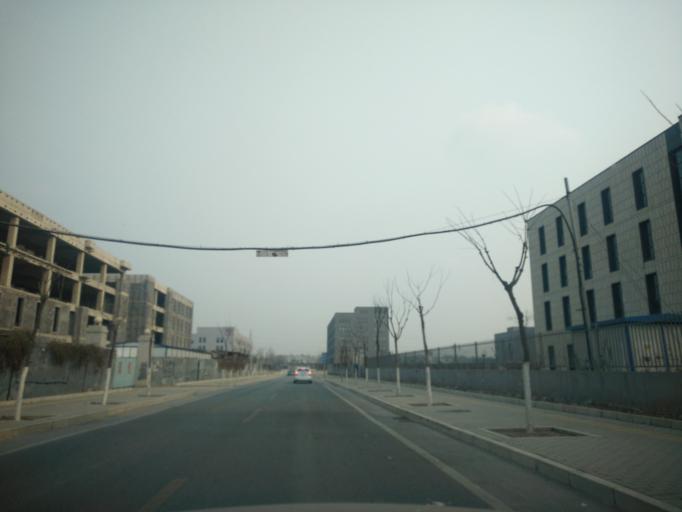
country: CN
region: Beijing
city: Yinghai
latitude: 39.7376
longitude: 116.4245
